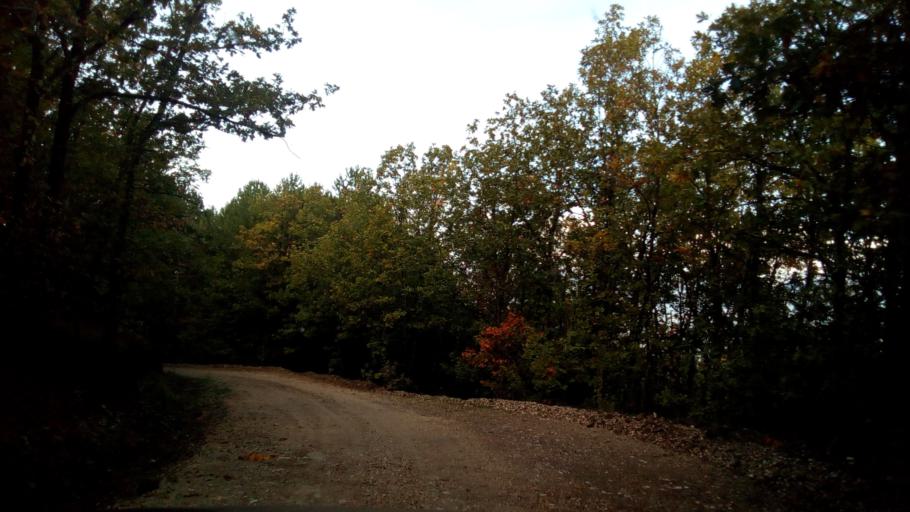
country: GR
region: West Greece
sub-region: Nomos Achaias
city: Kamarai
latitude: 38.4796
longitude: 22.0233
